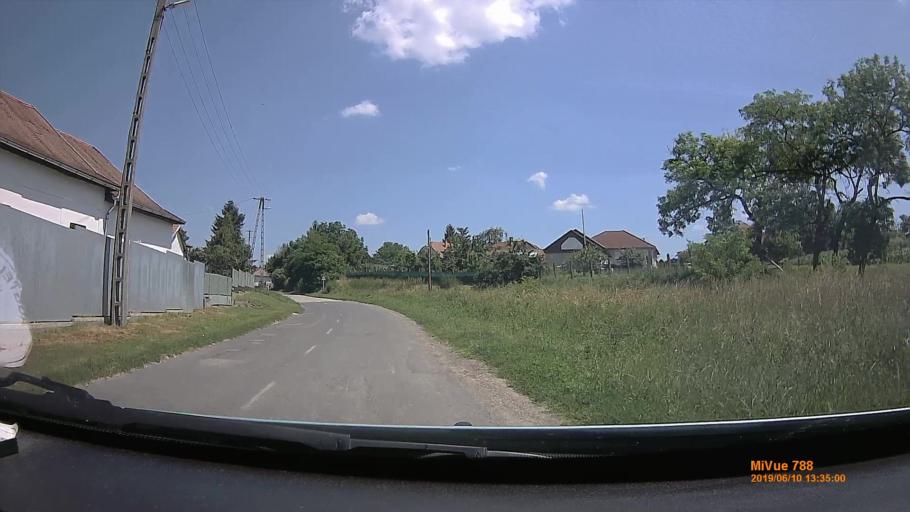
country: HU
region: Szabolcs-Szatmar-Bereg
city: Tiszadob
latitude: 48.0105
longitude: 21.1608
